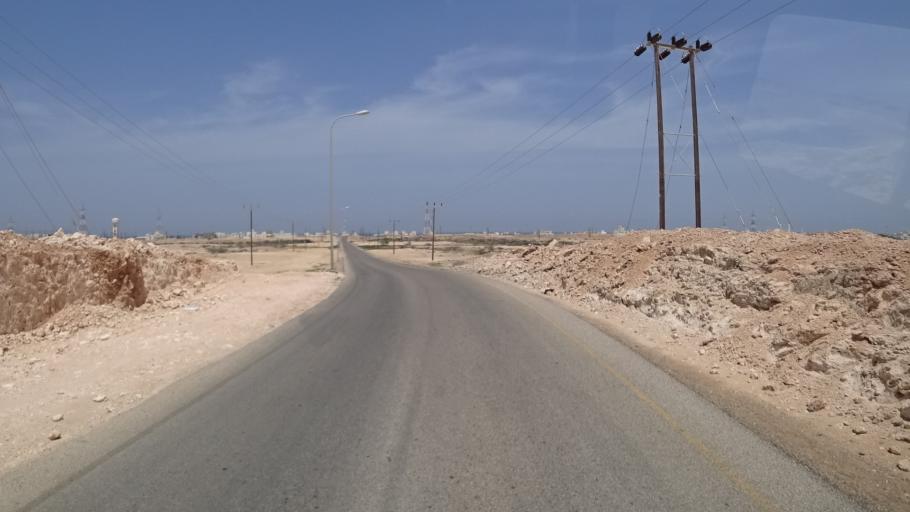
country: OM
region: Ash Sharqiyah
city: Sur
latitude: 22.6109
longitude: 59.4512
